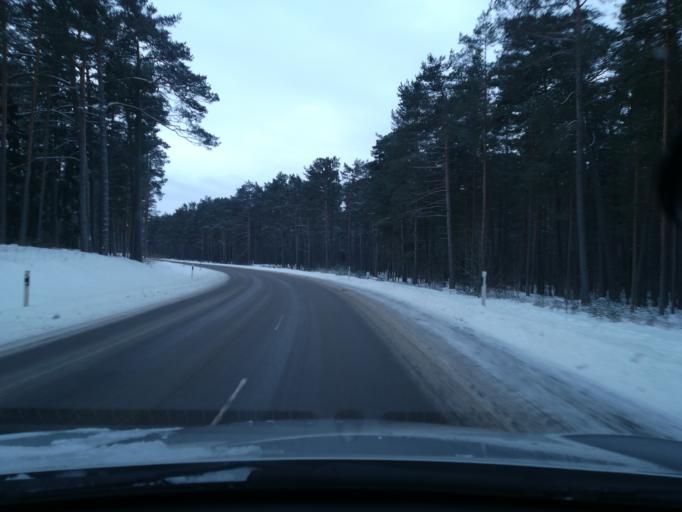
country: EE
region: Harju
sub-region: Keila linn
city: Keila
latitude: 59.4304
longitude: 24.3619
